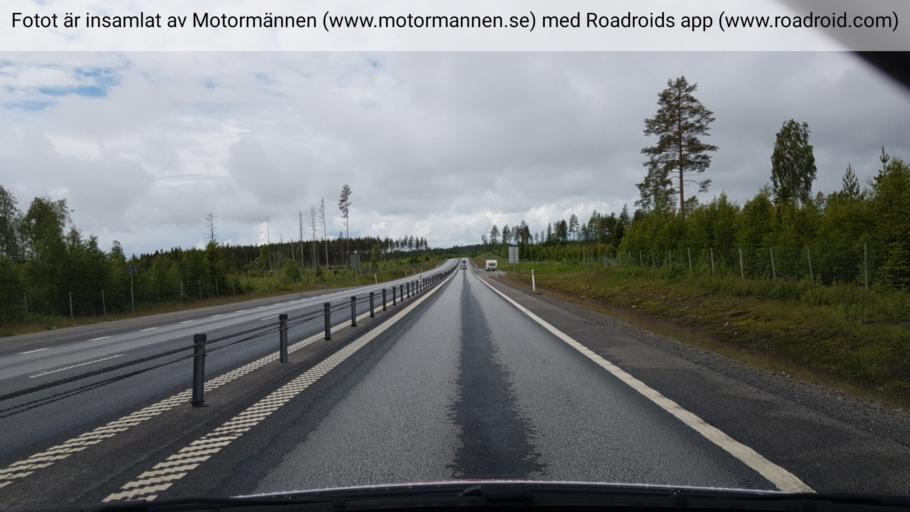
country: SE
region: Vaesterbotten
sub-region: Umea Kommun
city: Hoernefors
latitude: 63.6702
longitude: 19.9763
